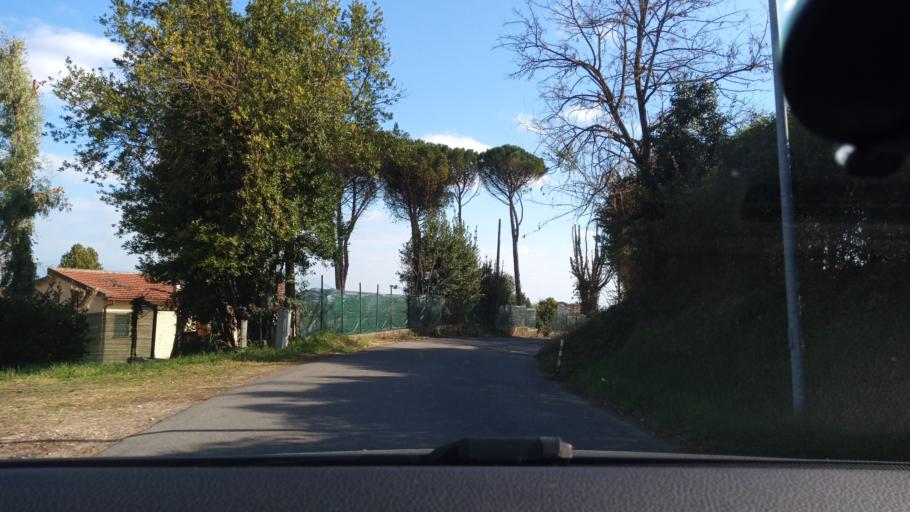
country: IT
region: Latium
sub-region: Citta metropolitana di Roma Capitale
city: Torrita Tiberina
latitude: 42.2424
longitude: 12.6141
